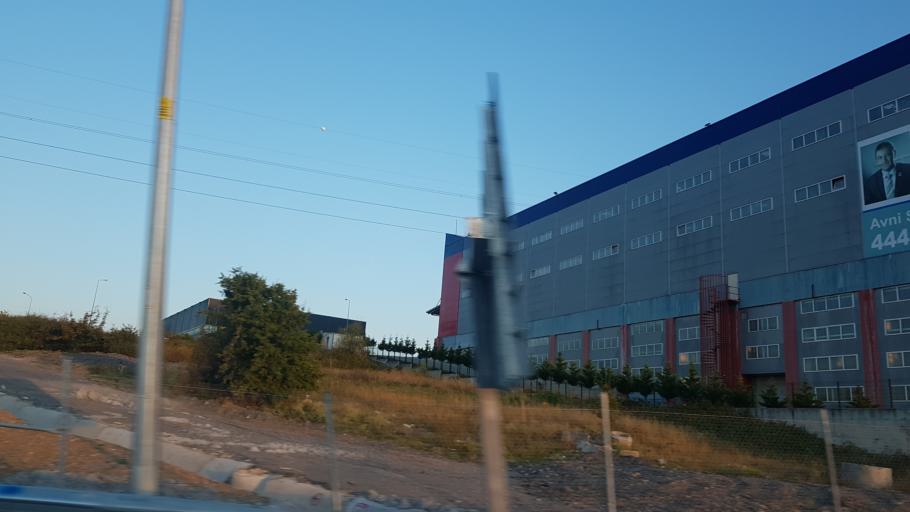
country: TR
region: Kocaeli
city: Tavsanli
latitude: 40.8025
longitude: 29.5195
